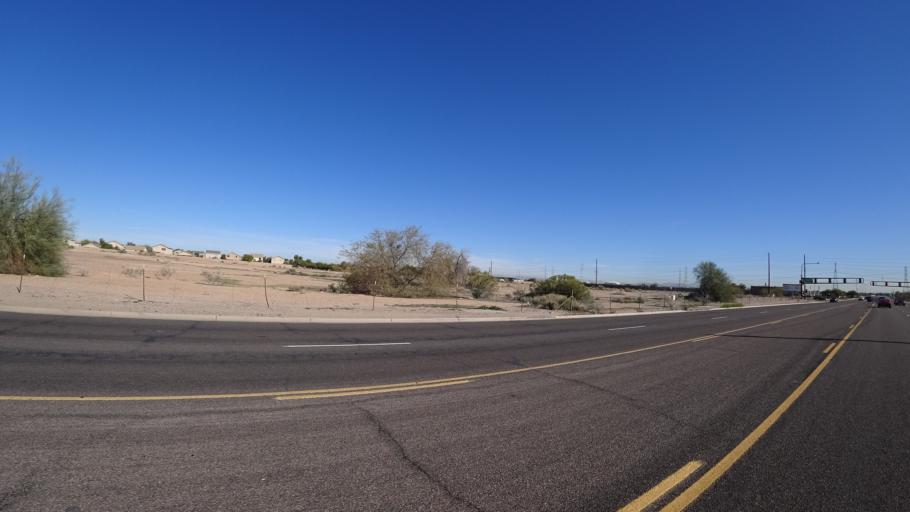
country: US
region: Arizona
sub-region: Maricopa County
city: Litchfield Park
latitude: 33.4932
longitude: -112.3255
